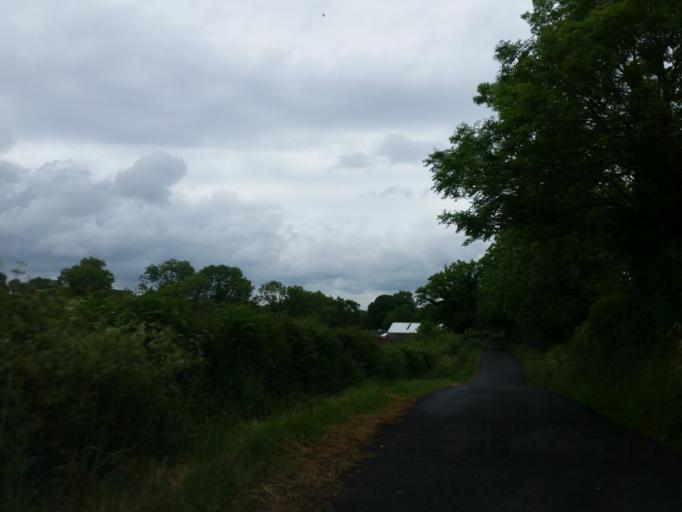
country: IE
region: Ulster
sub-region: County Monaghan
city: Clones
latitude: 54.2034
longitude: -7.2467
